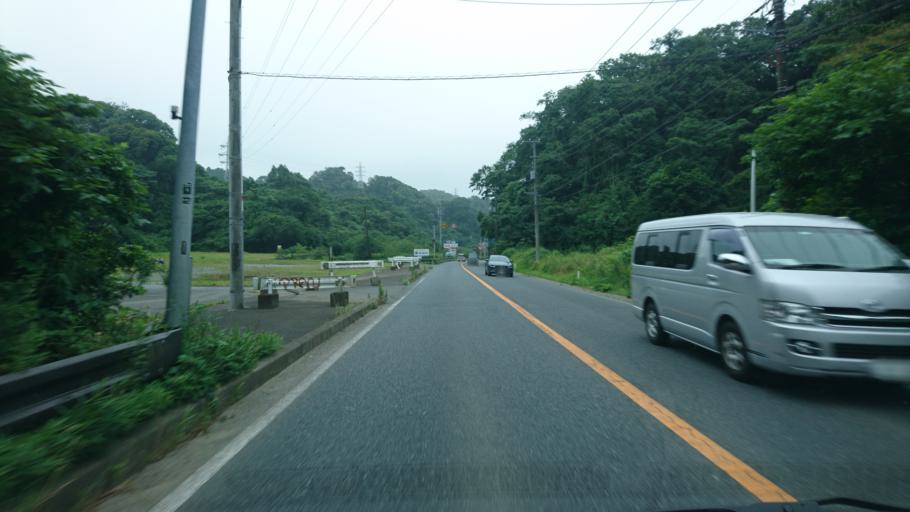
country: JP
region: Chiba
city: Kimitsu
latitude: 35.2785
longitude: 139.9106
